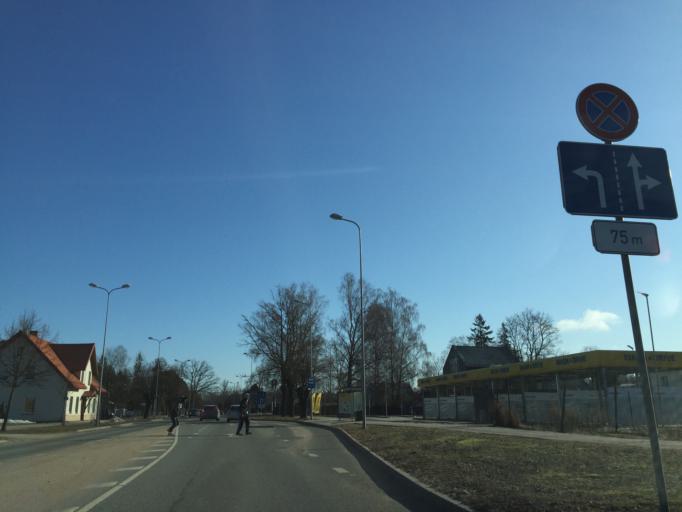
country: LV
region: Valmieras Rajons
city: Valmiera
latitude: 57.5325
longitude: 25.3965
